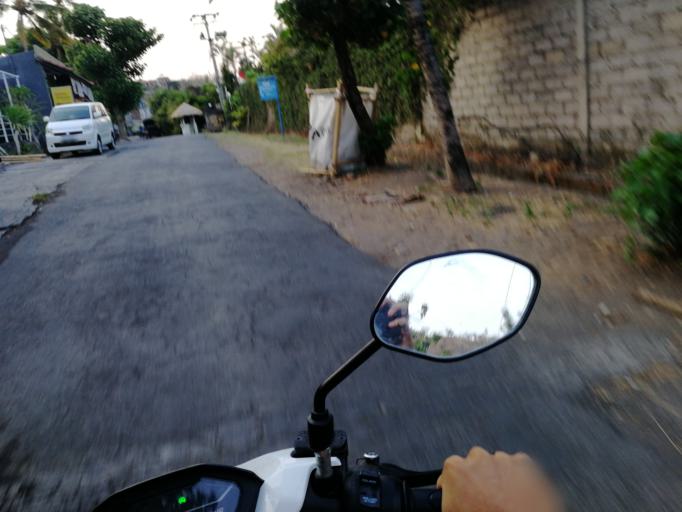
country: ID
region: Bali
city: Biaslantang Kaler
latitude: -8.3509
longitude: 115.6824
